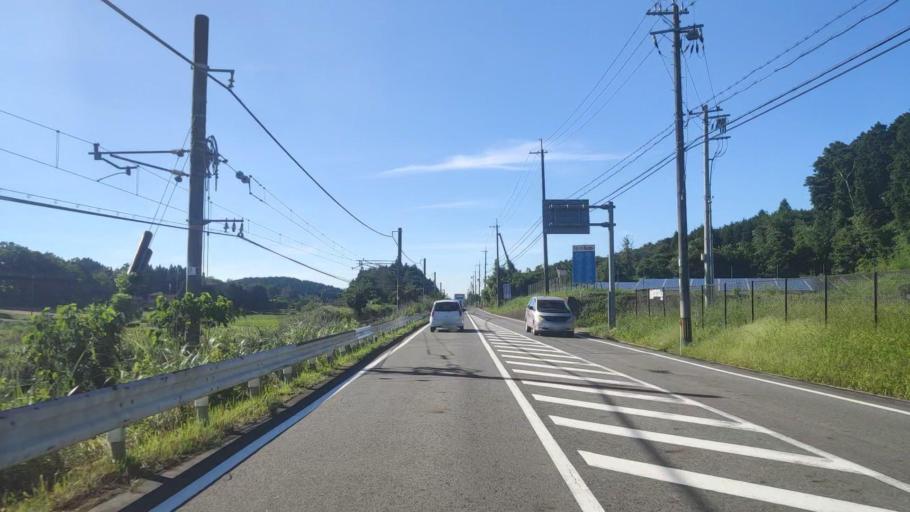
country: JP
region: Shiga Prefecture
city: Minakuchicho-matoba
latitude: 34.8771
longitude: 136.2387
